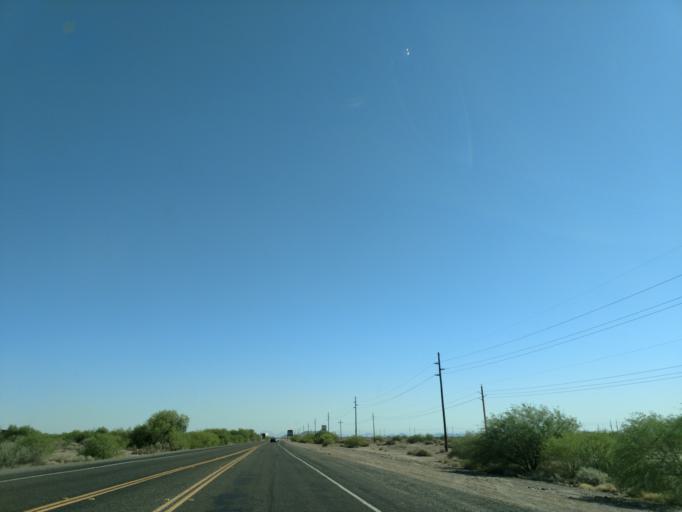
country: US
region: Arizona
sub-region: Maricopa County
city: Guadalupe
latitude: 33.2609
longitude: -111.9750
